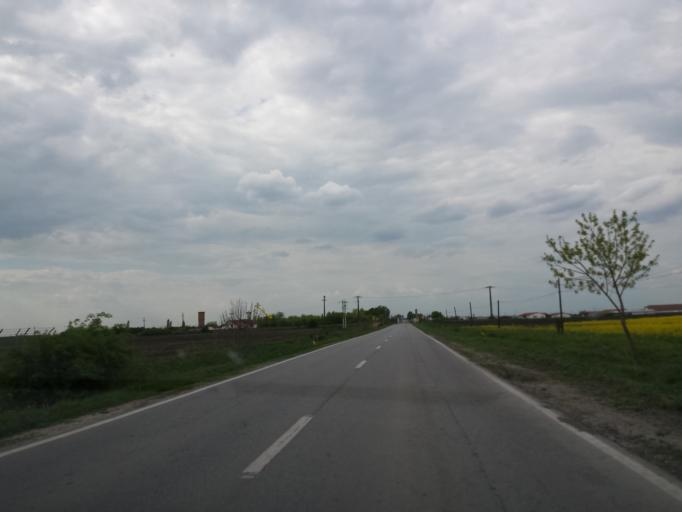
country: RO
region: Timis
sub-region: Comuna Sanpetru Mare
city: Sanpetru Mare
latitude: 46.0465
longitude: 20.6499
